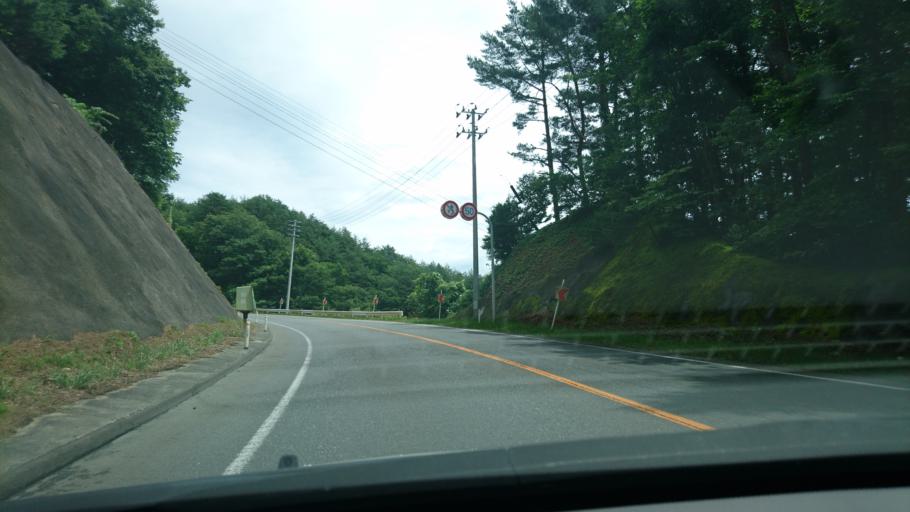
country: JP
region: Iwate
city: Miyako
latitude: 39.7047
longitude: 141.9601
